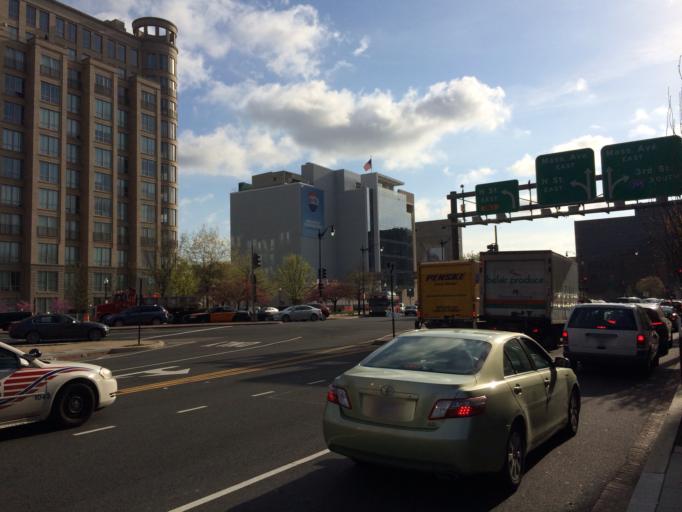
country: US
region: Washington, D.C.
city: Washington, D.C.
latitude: 38.8997
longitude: -77.0162
